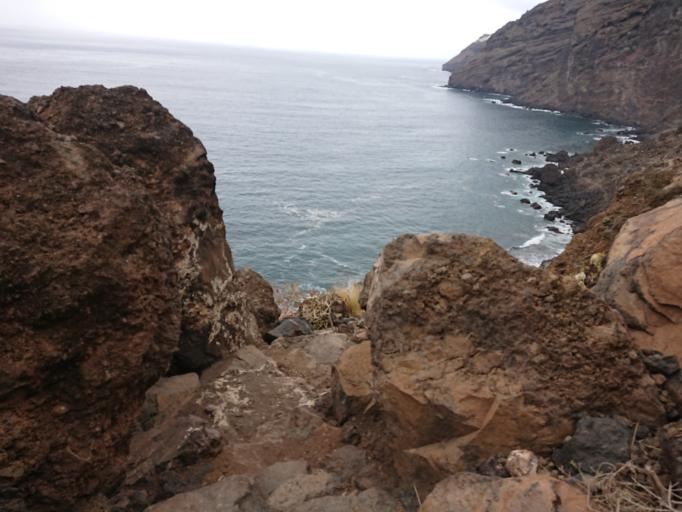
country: ES
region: Canary Islands
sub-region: Provincia de Santa Cruz de Tenerife
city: Tijarafe
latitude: 28.7198
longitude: -17.9790
